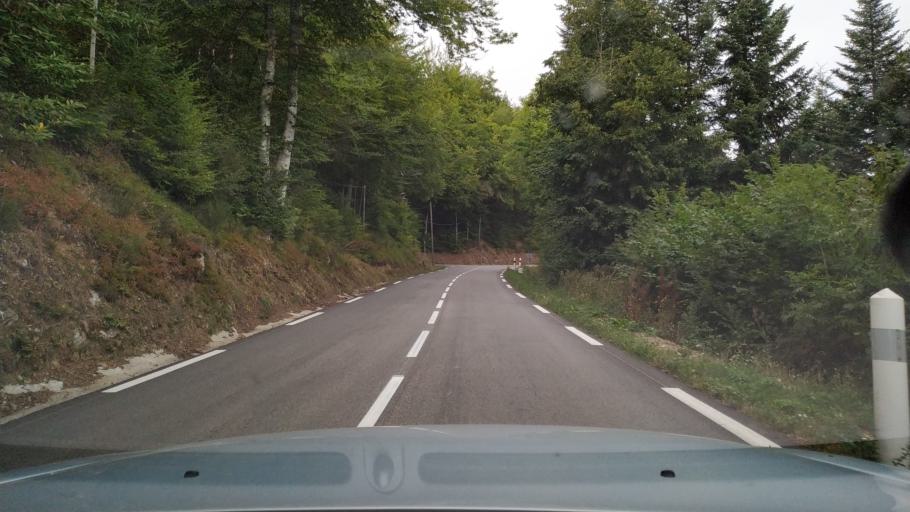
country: FR
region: Rhone-Alpes
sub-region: Departement de l'Ardeche
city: Saint-Agreve
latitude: 45.0017
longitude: 4.4098
